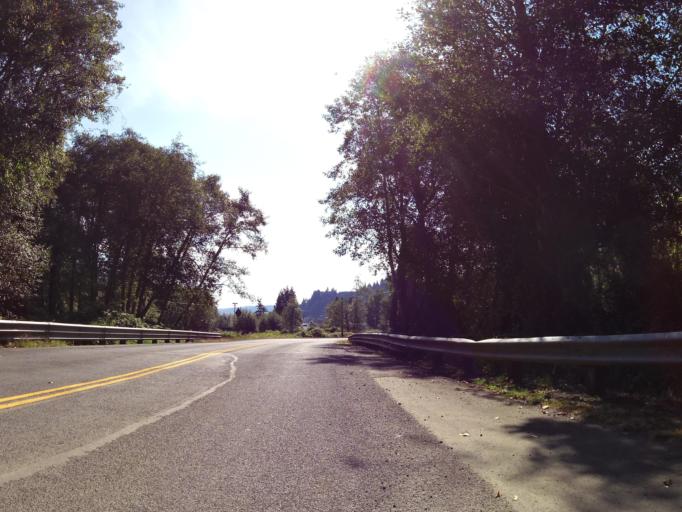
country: US
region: Washington
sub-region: Wahkiakum County
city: Cathlamet
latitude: 46.1356
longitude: -123.3765
